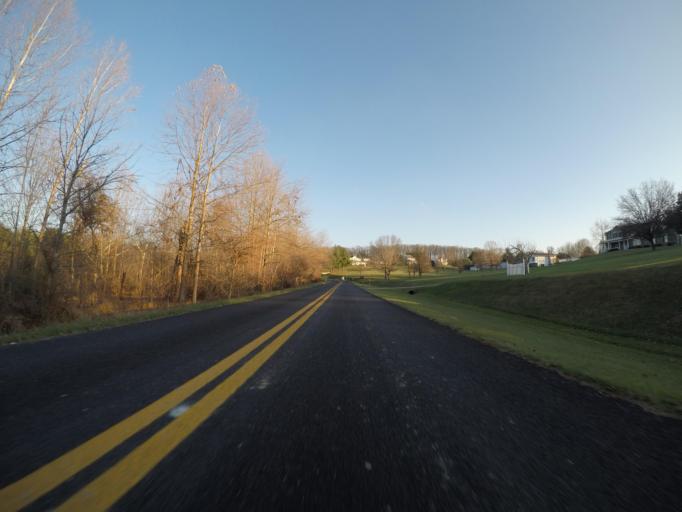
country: US
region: Maryland
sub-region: Carroll County
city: Hampstead
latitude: 39.5885
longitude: -76.8735
